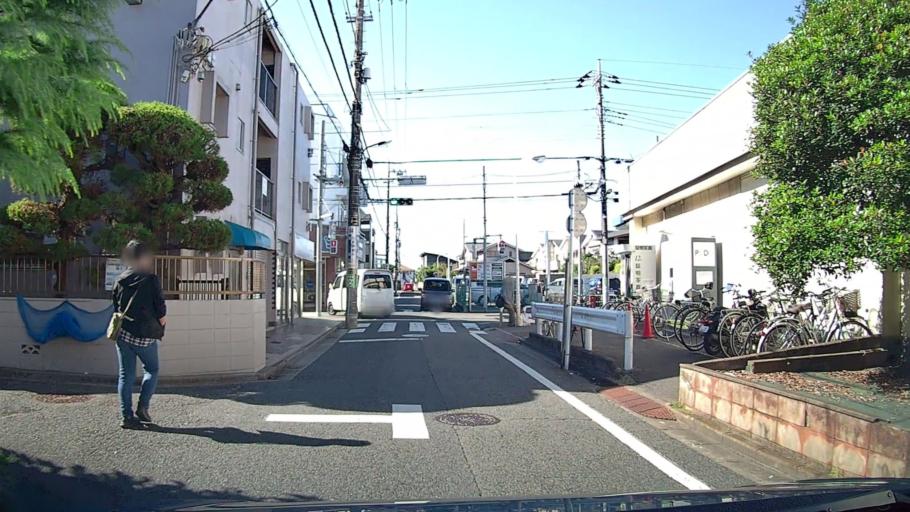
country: JP
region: Tokyo
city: Nishi-Tokyo-shi
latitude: 35.7504
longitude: 139.5704
